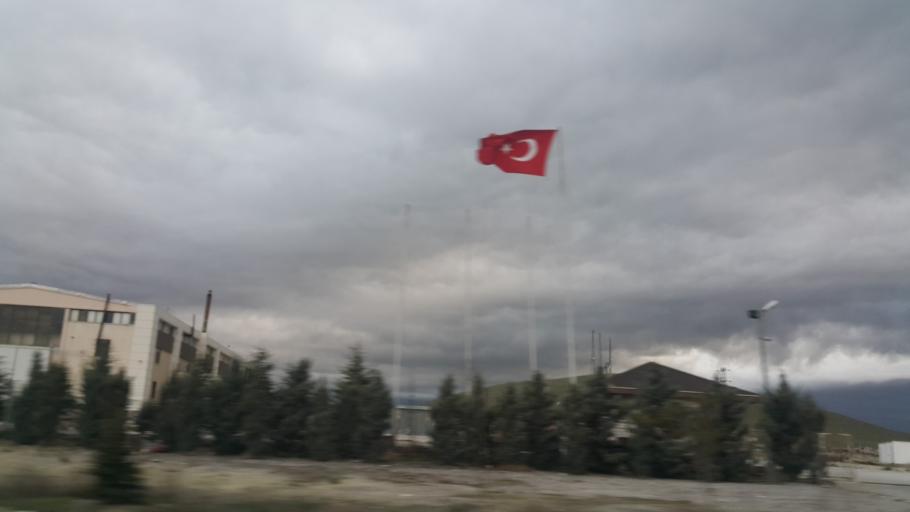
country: TR
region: Ankara
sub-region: Goelbasi
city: Golbasi
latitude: 39.6486
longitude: 32.8186
